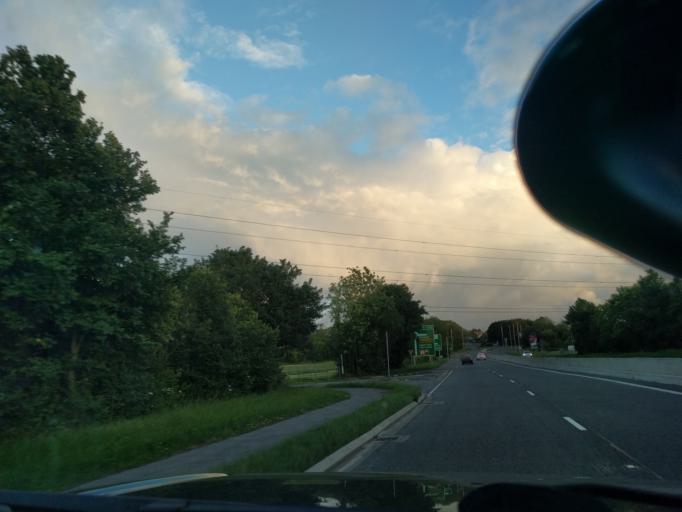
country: GB
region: England
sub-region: Wiltshire
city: Chippenham
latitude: 51.4809
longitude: -2.1286
